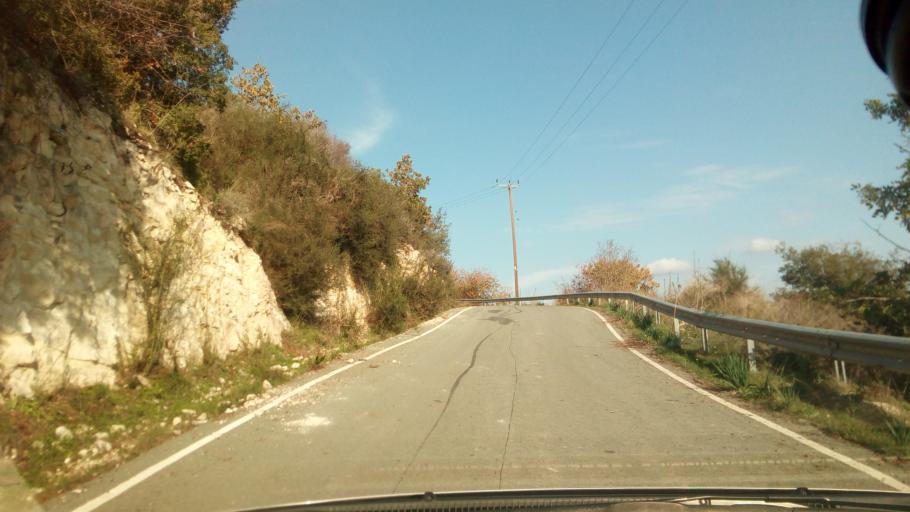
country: CY
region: Pafos
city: Polis
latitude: 34.9534
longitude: 32.4269
